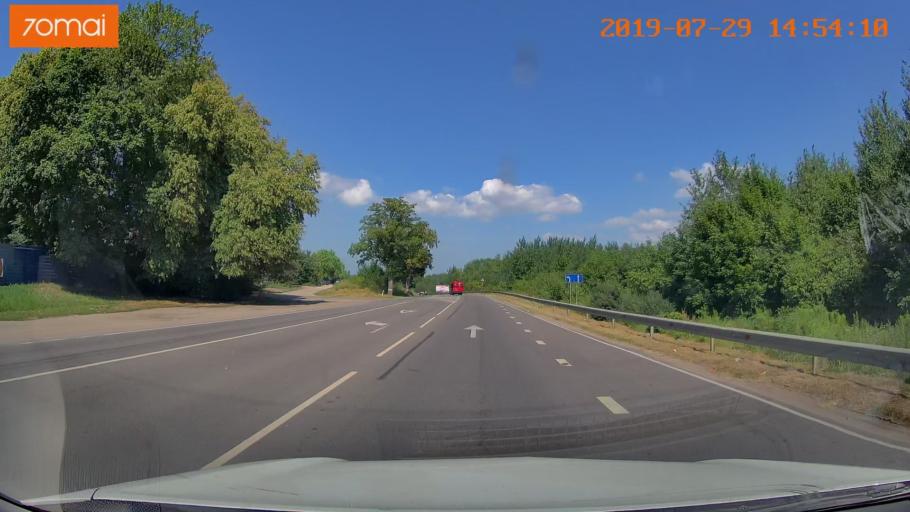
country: RU
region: Kaliningrad
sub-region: Gorod Kaliningrad
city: Baltiysk
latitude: 54.6716
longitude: 19.9228
